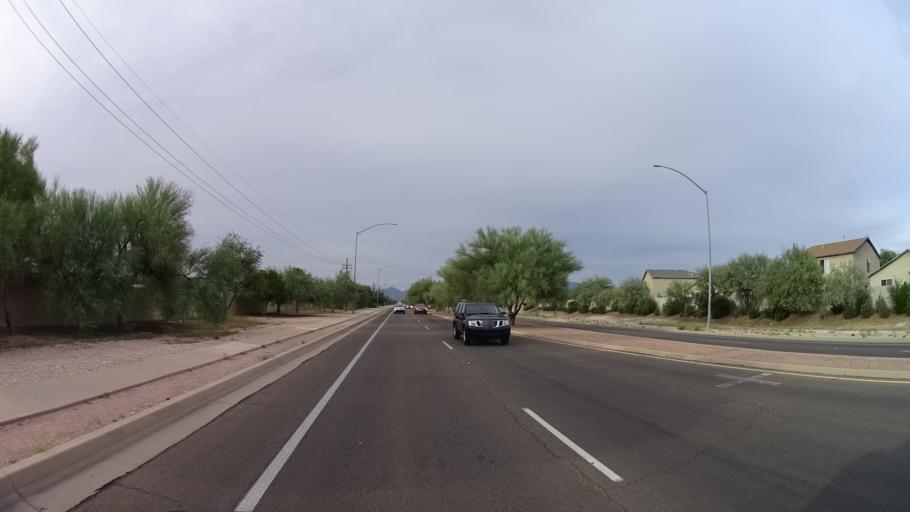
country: US
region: Arizona
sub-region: Pima County
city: South Tucson
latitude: 32.1567
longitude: -110.9351
